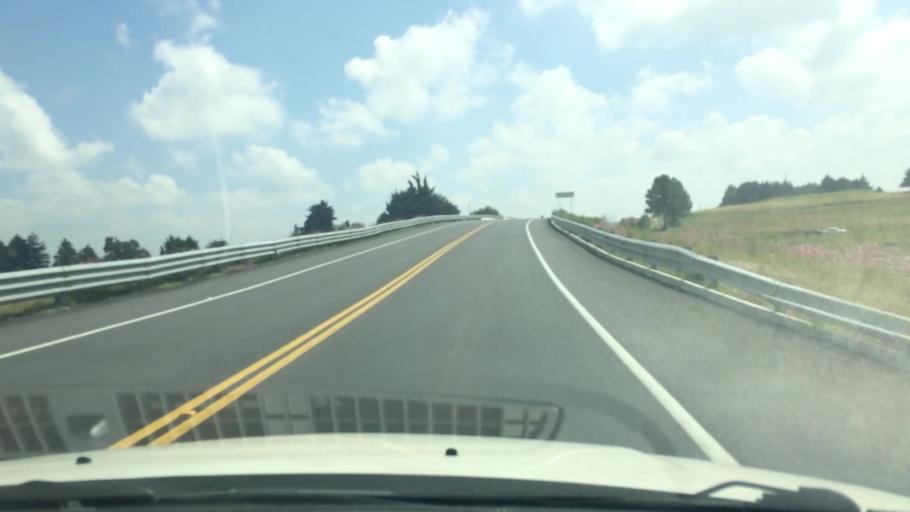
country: MX
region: Mexico
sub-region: Villa Victoria
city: Colonia Doctor Gustavo Baz
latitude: 19.3723
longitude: -99.9296
